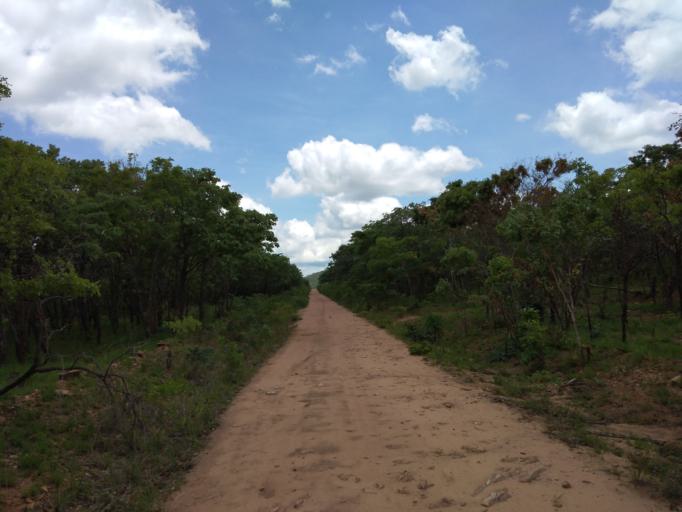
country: ZM
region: Central
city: Mkushi
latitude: -13.9075
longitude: 29.8648
